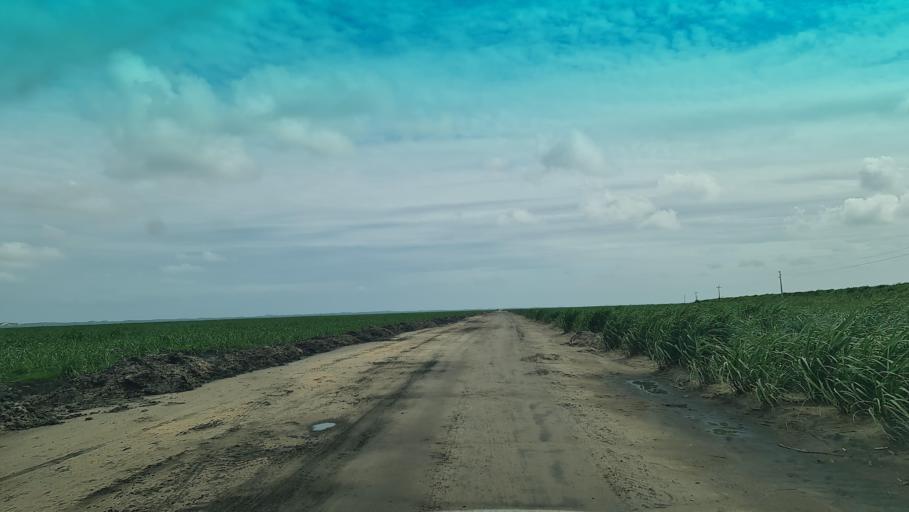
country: MZ
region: Maputo
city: Manhica
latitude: -25.4660
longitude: 32.8178
